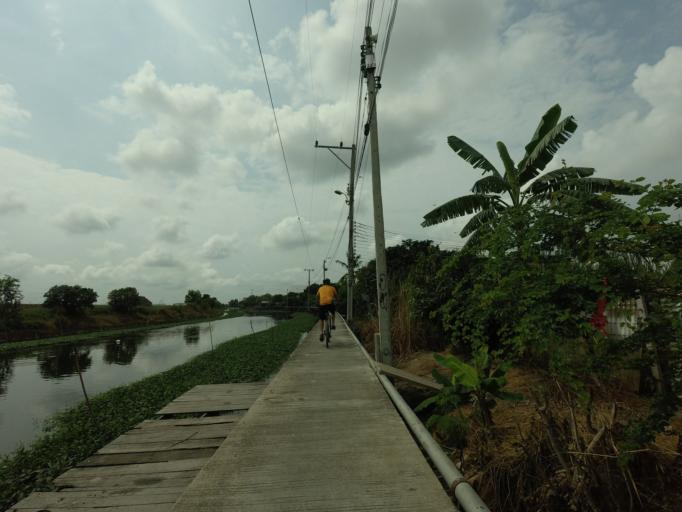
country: TH
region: Bangkok
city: Lat Krabang
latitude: 13.6677
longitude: 100.7249
